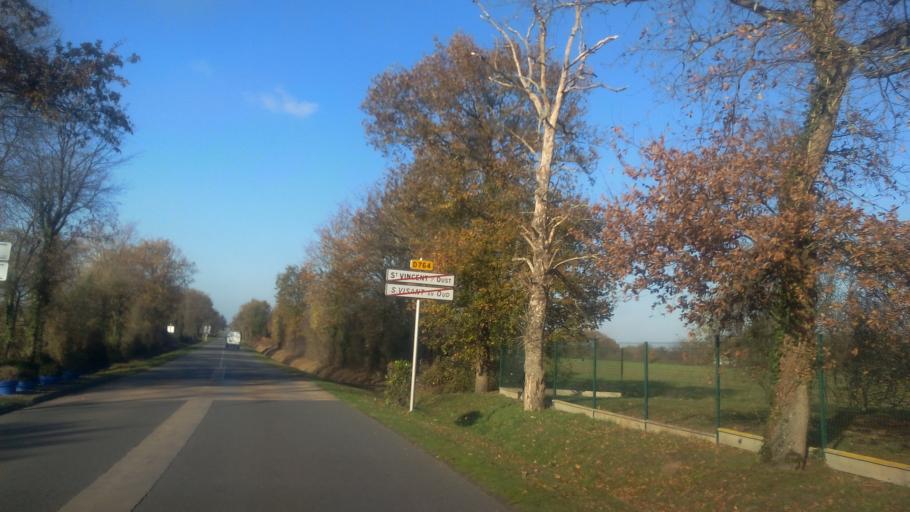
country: FR
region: Brittany
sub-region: Departement du Morbihan
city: Saint-Vincent-sur-Oust
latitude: 47.7024
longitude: -2.1500
